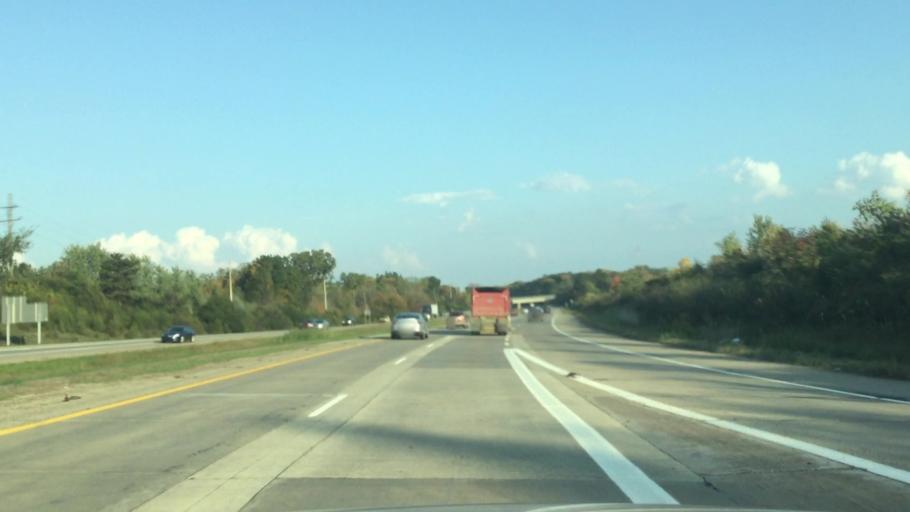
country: US
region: Michigan
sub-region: Washtenaw County
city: Ann Arbor
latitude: 42.3008
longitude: -83.7751
